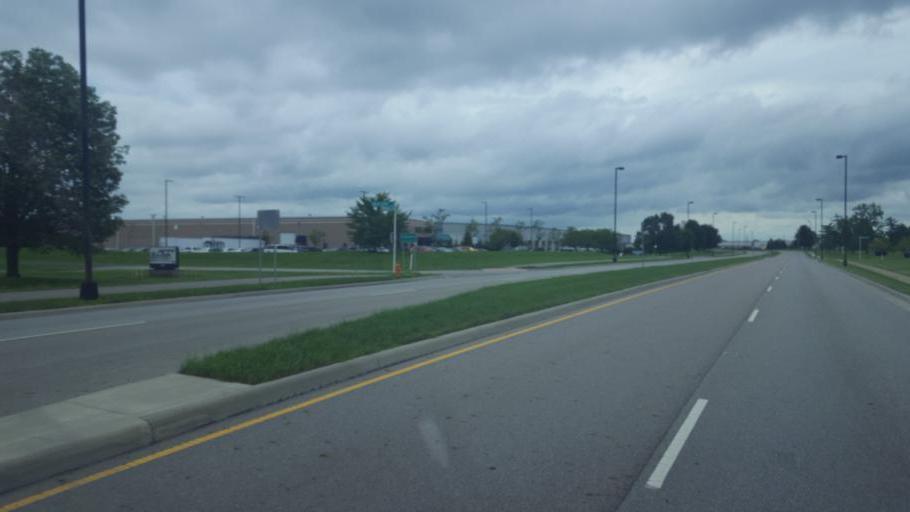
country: US
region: Ohio
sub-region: Franklin County
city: Obetz
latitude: 39.8230
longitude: -82.9397
